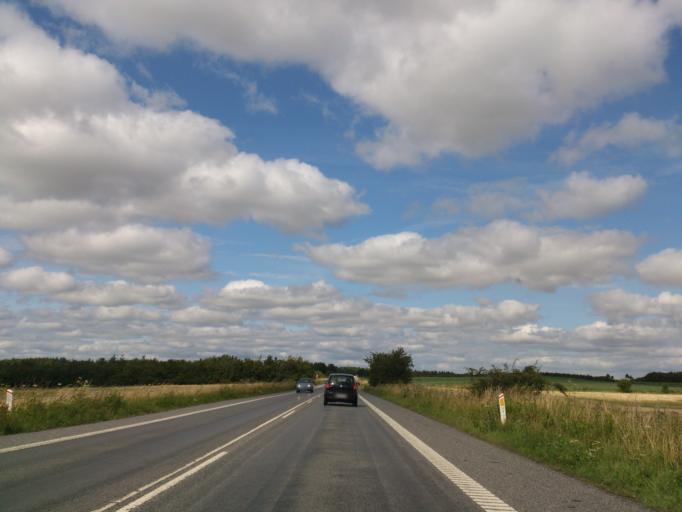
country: DK
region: South Denmark
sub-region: Aabenraa Kommune
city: Krusa
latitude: 54.8941
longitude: 9.4282
